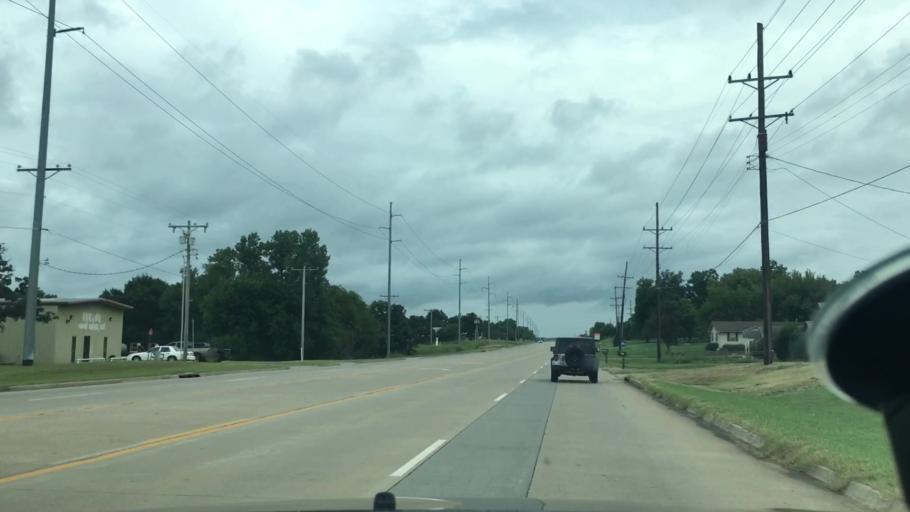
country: US
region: Oklahoma
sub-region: Seminole County
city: Seminole
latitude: 35.2597
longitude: -96.6711
